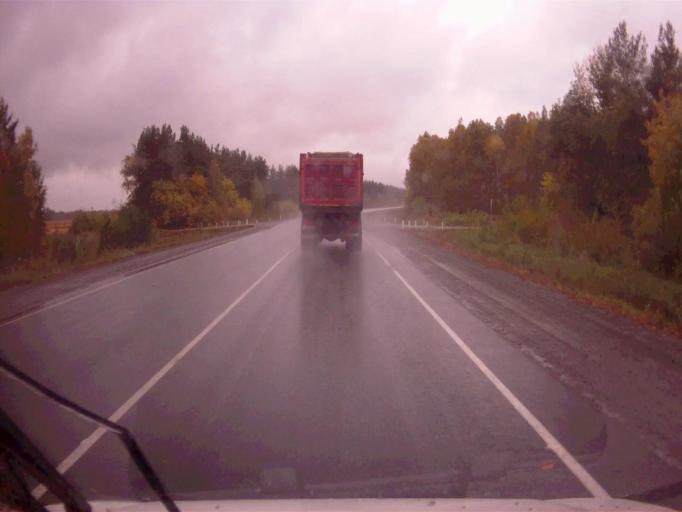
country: RU
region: Chelyabinsk
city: Roshchino
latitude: 55.3574
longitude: 61.2392
